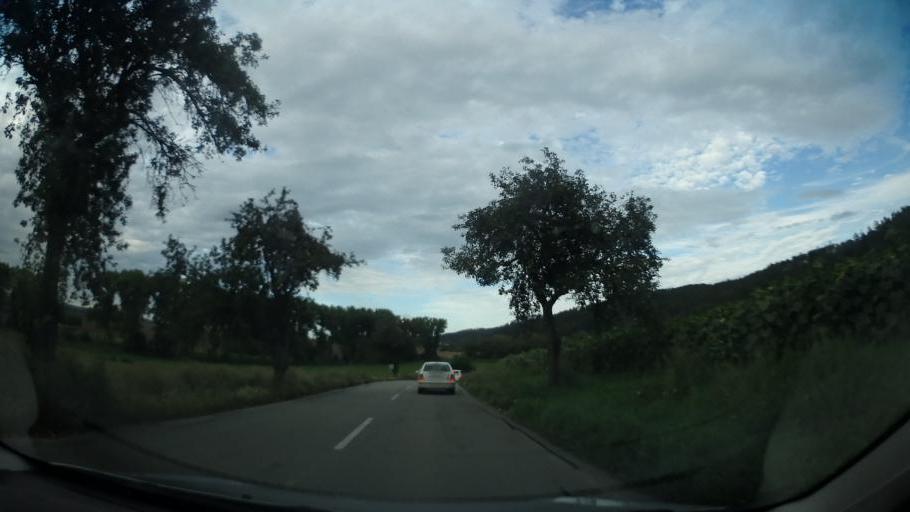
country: CZ
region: South Moravian
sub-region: Okres Blansko
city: Boskovice
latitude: 49.5124
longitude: 16.6759
